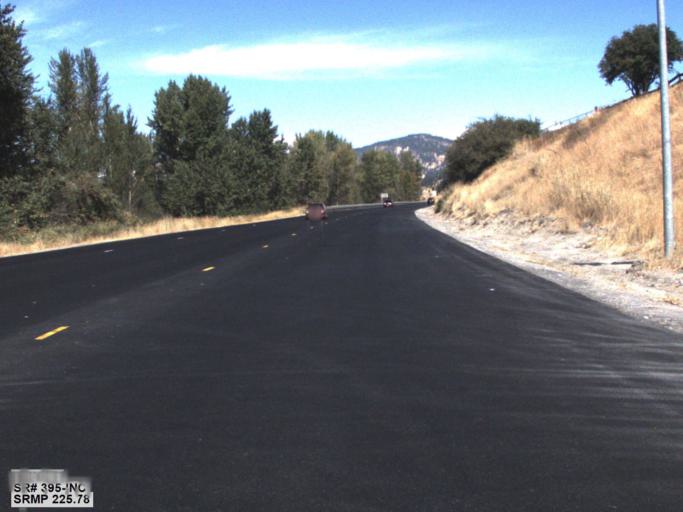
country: US
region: Washington
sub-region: Stevens County
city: Colville
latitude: 48.4915
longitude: -117.9030
